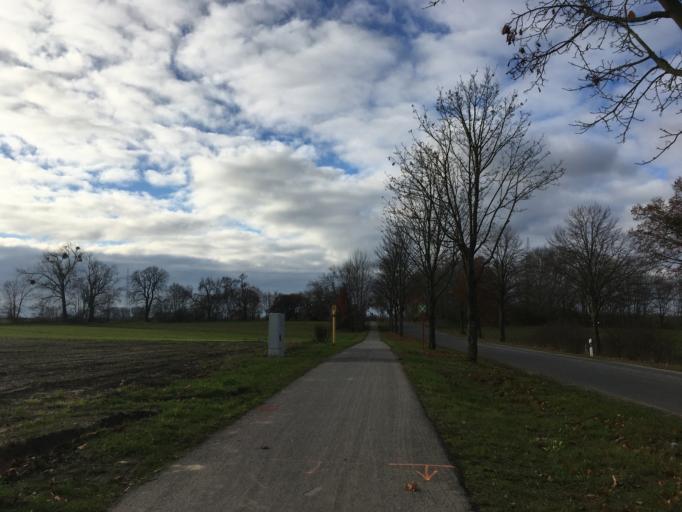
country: DE
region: Brandenburg
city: Rehfelde
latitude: 52.5336
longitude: 13.9605
